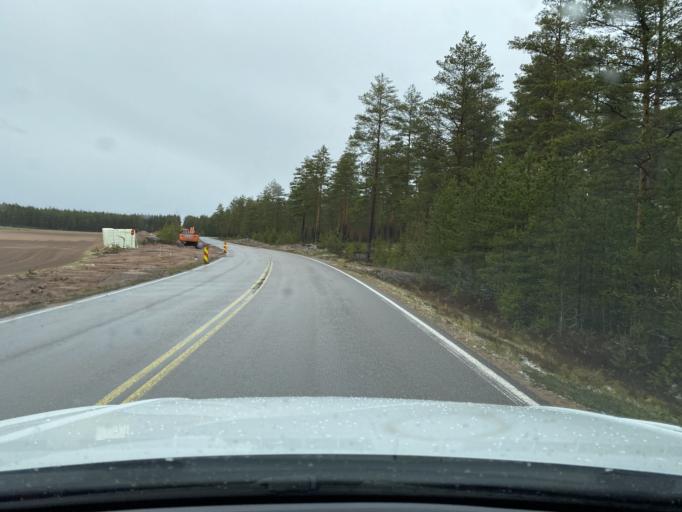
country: FI
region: Satakunta
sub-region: Pori
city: Vampula
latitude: 60.9618
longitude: 22.6769
